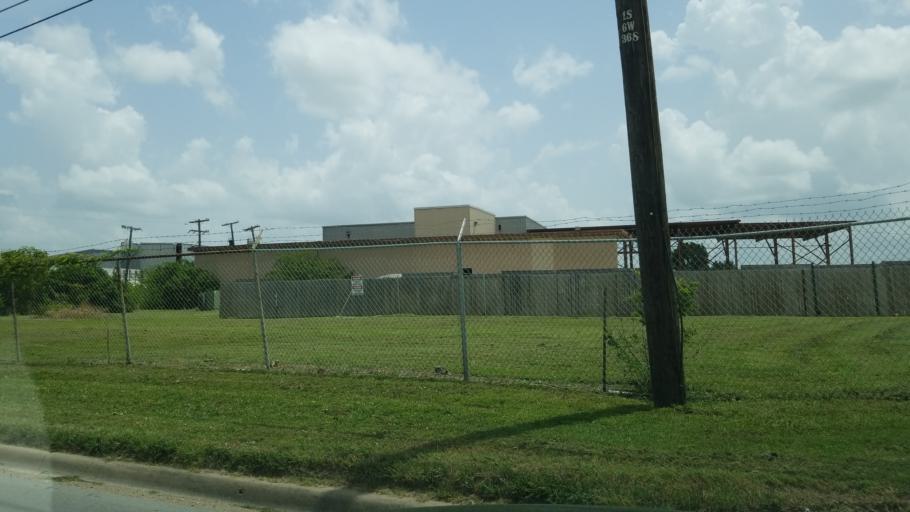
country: US
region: Texas
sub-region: Dallas County
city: Cockrell Hill
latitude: 32.7784
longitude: -96.8947
